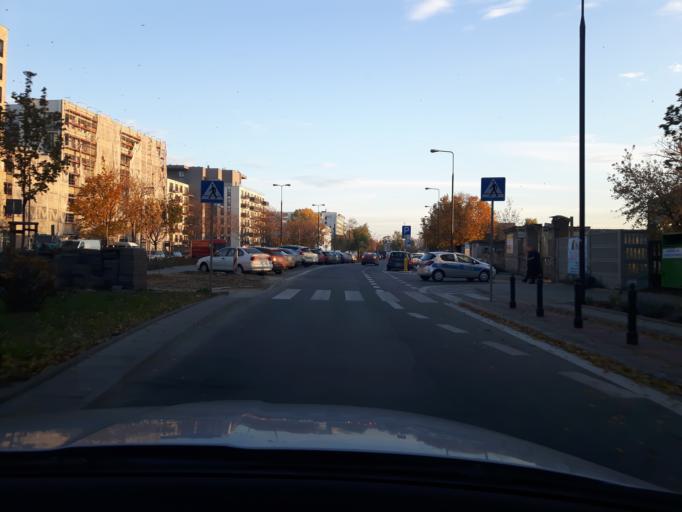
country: PL
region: Masovian Voivodeship
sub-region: Warszawa
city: Ochota
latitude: 52.2248
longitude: 20.9528
